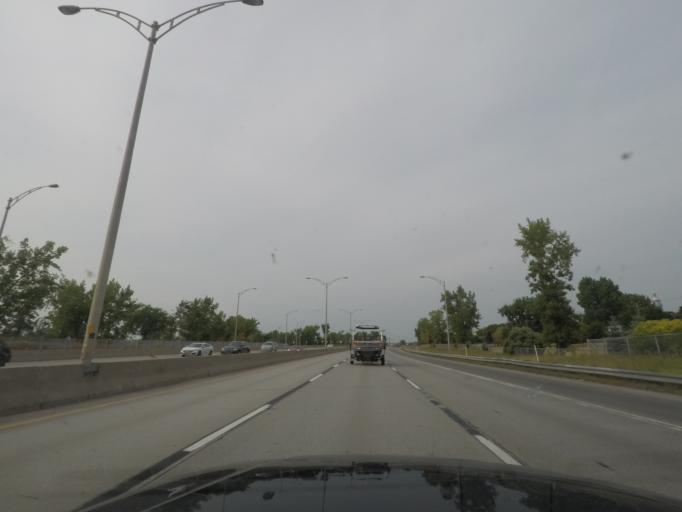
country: CA
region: Quebec
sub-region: Monteregie
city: La Prairie
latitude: 45.4186
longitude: -73.4989
